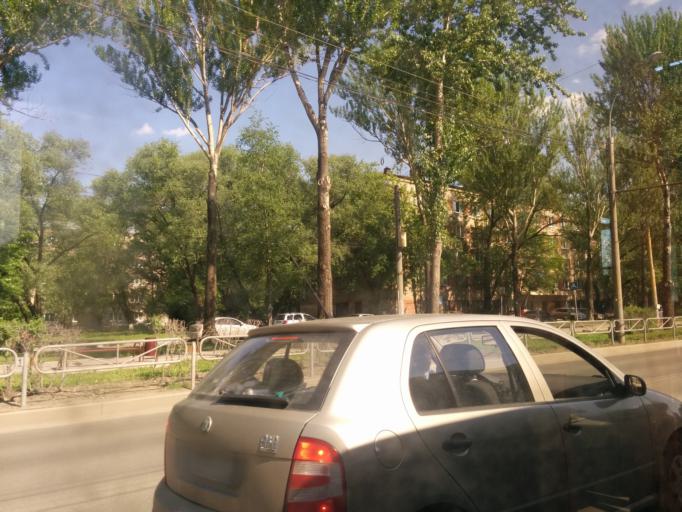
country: RU
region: Perm
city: Perm
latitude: 58.0082
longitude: 56.2829
